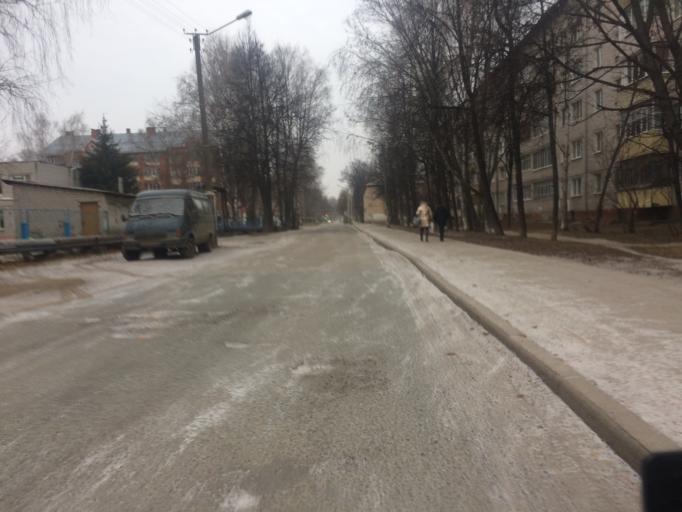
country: RU
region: Mariy-El
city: Yoshkar-Ola
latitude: 56.6431
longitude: 47.8953
